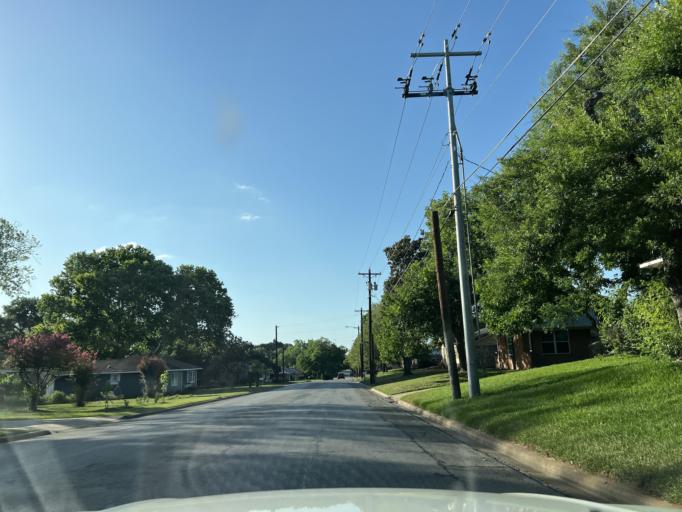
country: US
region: Texas
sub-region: Washington County
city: Brenham
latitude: 30.1589
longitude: -96.3874
